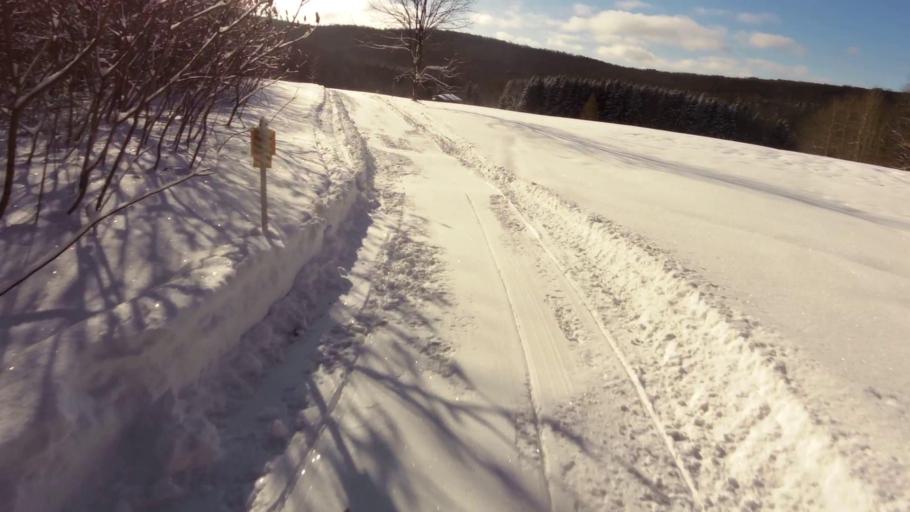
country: US
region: New York
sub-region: Chautauqua County
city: Falconer
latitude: 42.2566
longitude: -79.1709
